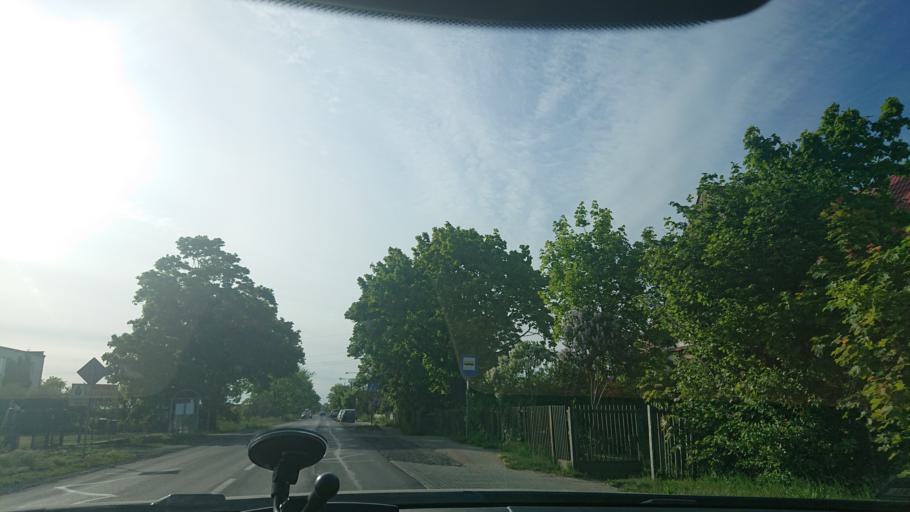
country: PL
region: Greater Poland Voivodeship
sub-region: Powiat gnieznienski
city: Gniezno
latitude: 52.5442
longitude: 17.5678
